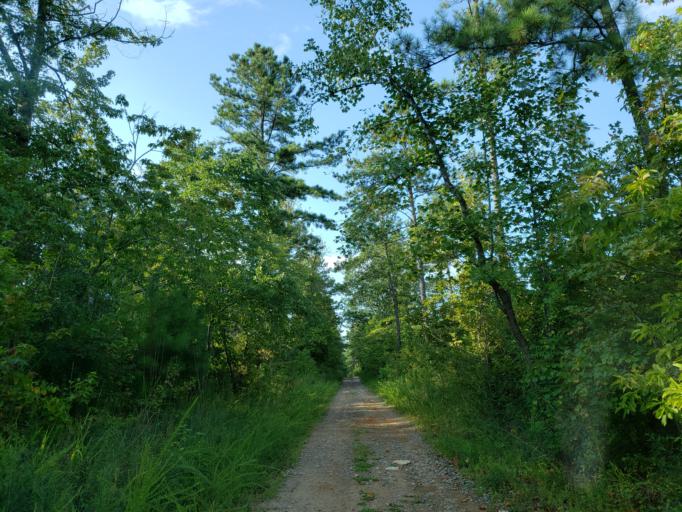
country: US
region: Georgia
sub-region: Cobb County
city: Acworth
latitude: 34.1732
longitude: -84.6447
